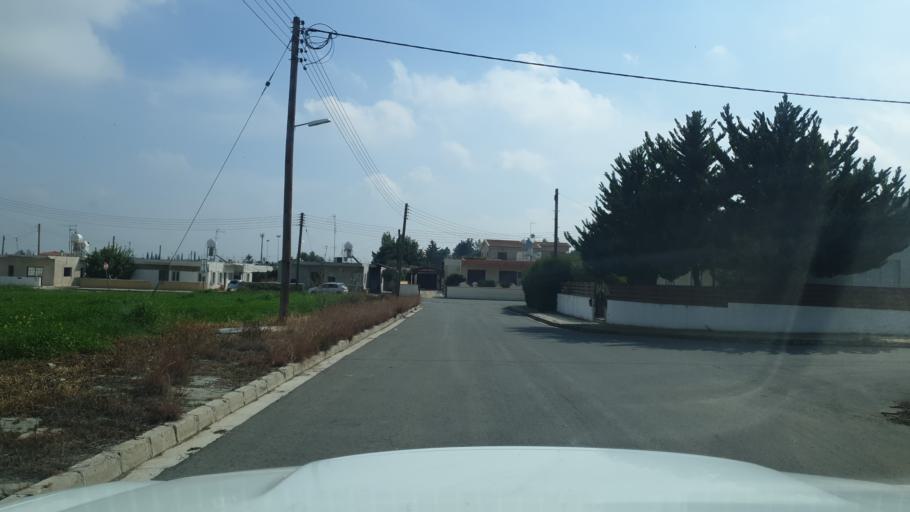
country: CY
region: Lefkosia
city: Kato Deftera
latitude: 35.0855
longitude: 33.2847
